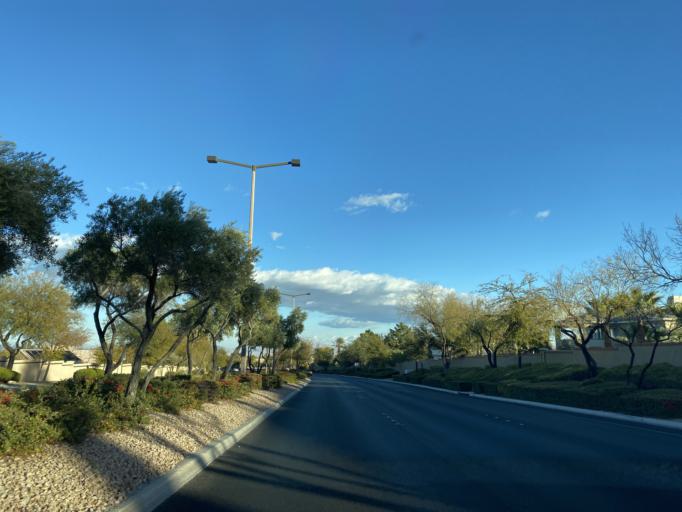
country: US
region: Nevada
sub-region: Clark County
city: Summerlin South
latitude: 36.2043
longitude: -115.3120
